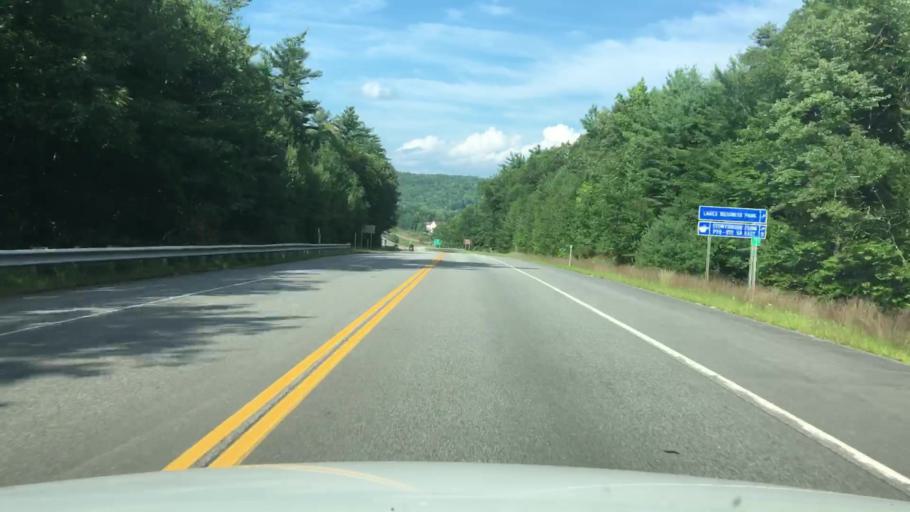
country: US
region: New Hampshire
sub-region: Belknap County
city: Laconia
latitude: 43.5246
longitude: -71.4456
